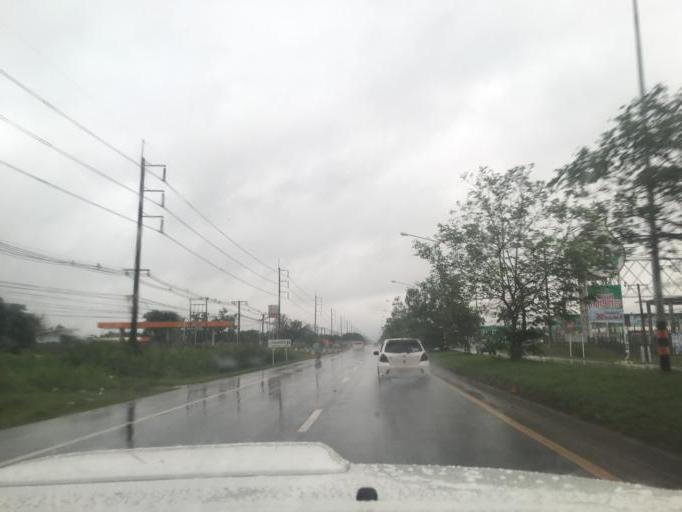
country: TH
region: Changwat Udon Thani
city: Udon Thani
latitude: 17.3785
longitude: 102.7412
